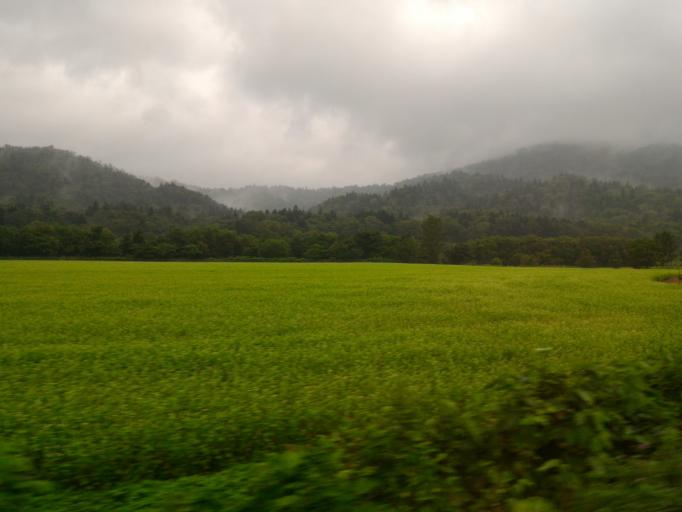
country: JP
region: Hokkaido
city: Nayoro
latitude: 44.7305
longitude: 142.0833
